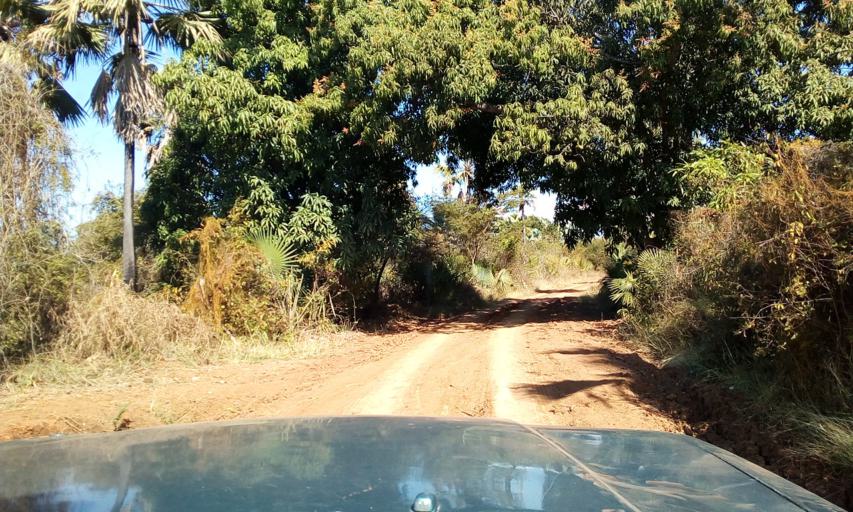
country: MG
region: Boeny
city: Mahajanga
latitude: -16.0531
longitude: 45.8104
